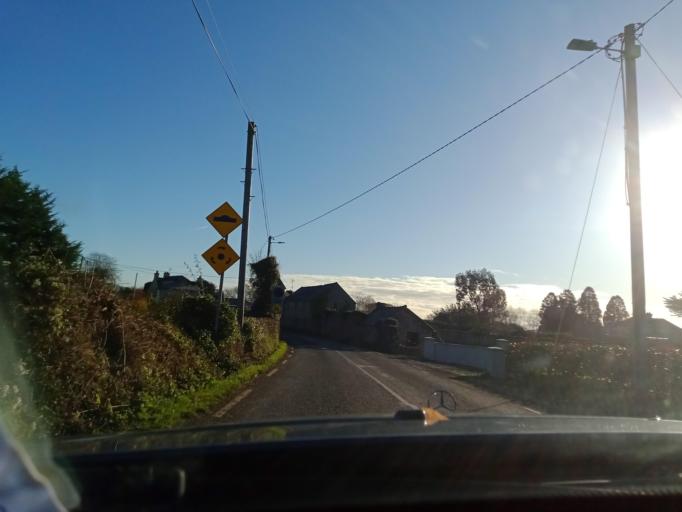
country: IE
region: Leinster
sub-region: Kilkenny
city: Piltown
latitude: 52.3882
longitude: -7.3456
